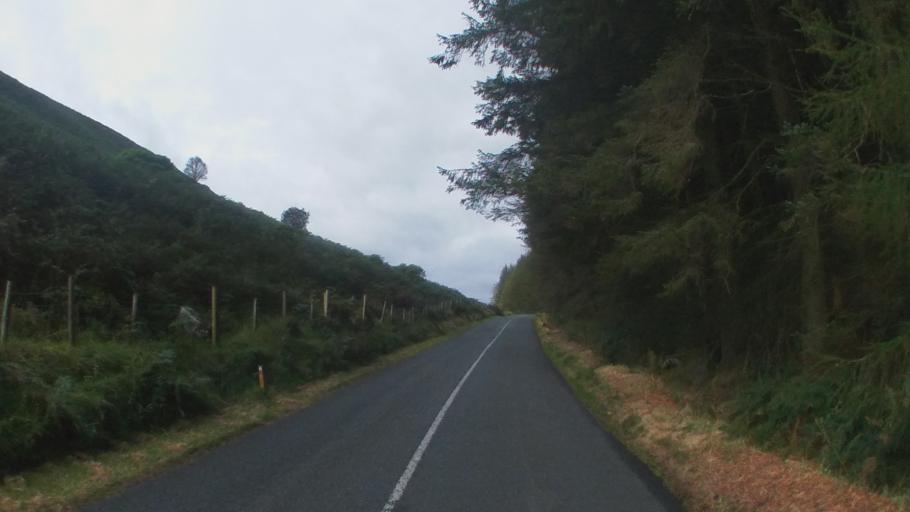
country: IE
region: Leinster
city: Ballinteer
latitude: 53.2349
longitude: -6.2803
